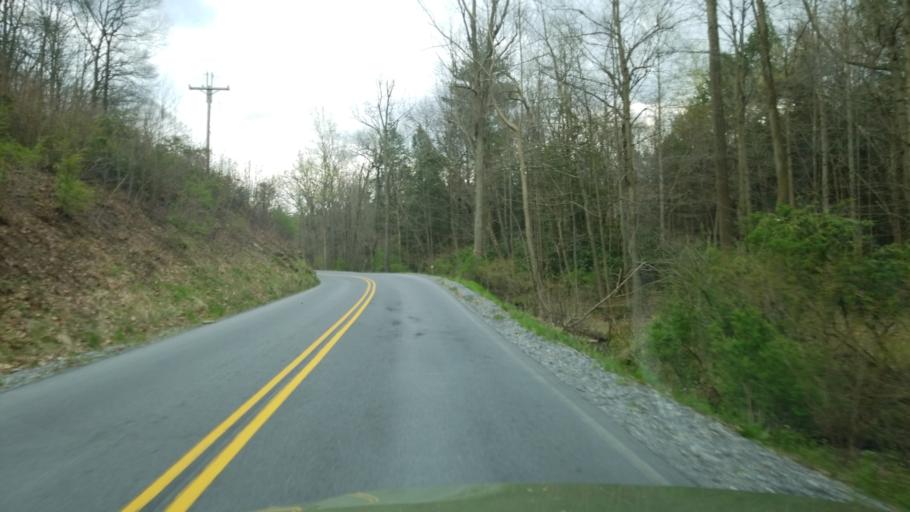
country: US
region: Pennsylvania
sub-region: Blair County
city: Tipton
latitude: 40.6543
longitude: -78.3275
